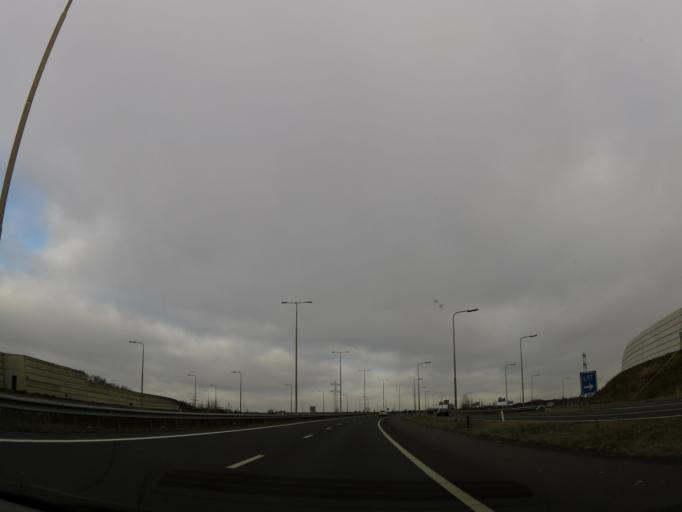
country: NL
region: Limburg
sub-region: Gemeente Venlo
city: Tegelen
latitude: 51.3813
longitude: 6.1230
